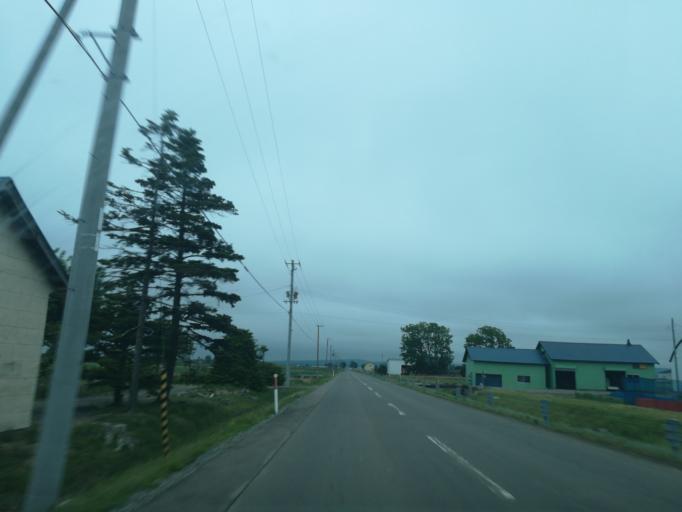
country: JP
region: Hokkaido
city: Iwamizawa
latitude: 43.1371
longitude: 141.7127
